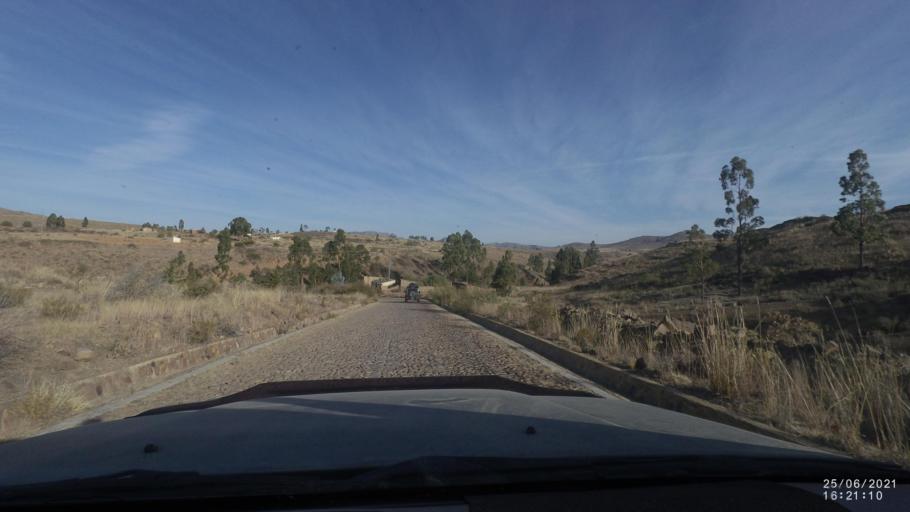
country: BO
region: Cochabamba
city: Cliza
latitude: -17.7510
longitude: -65.8384
